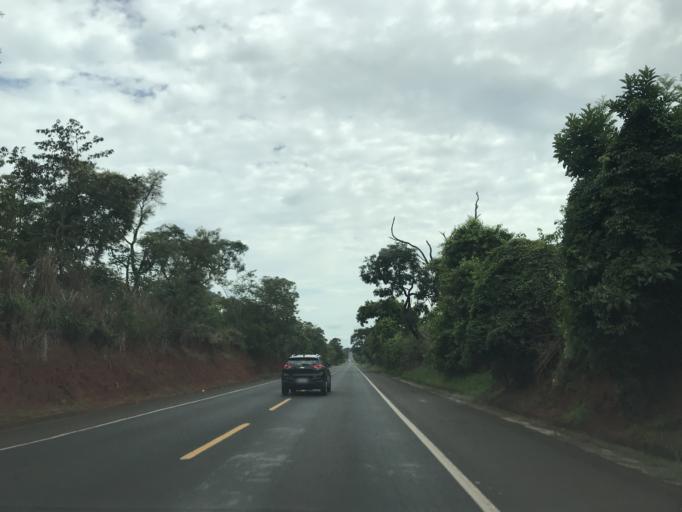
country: BR
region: Minas Gerais
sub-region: Frutal
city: Frutal
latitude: -19.9836
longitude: -49.0181
